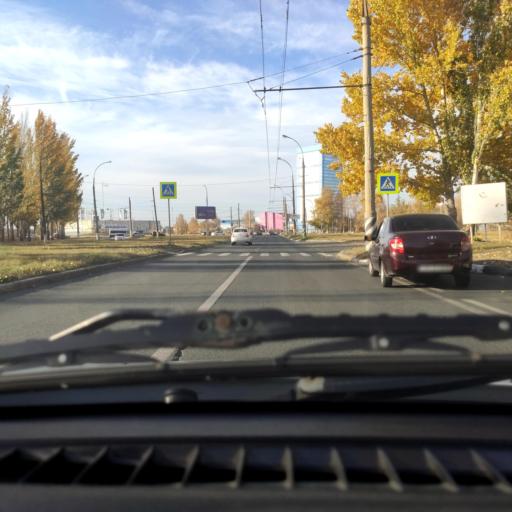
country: RU
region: Samara
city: Tol'yatti
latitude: 53.5512
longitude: 49.2697
